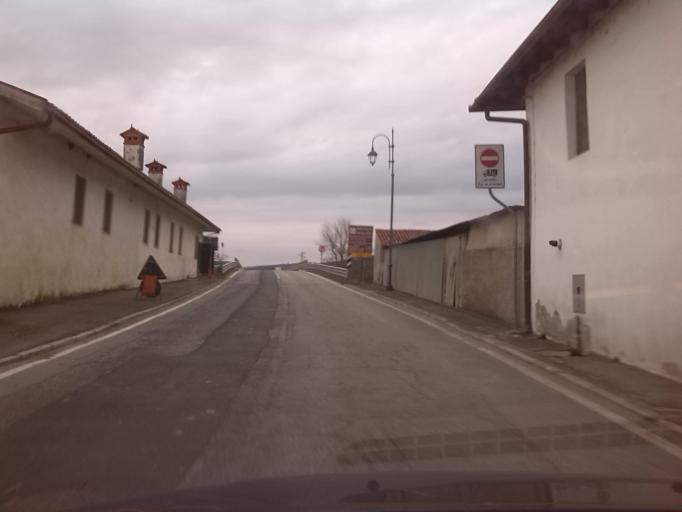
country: IT
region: Friuli Venezia Giulia
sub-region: Provincia di Gorizia
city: Medea
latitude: 45.9087
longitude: 13.4379
